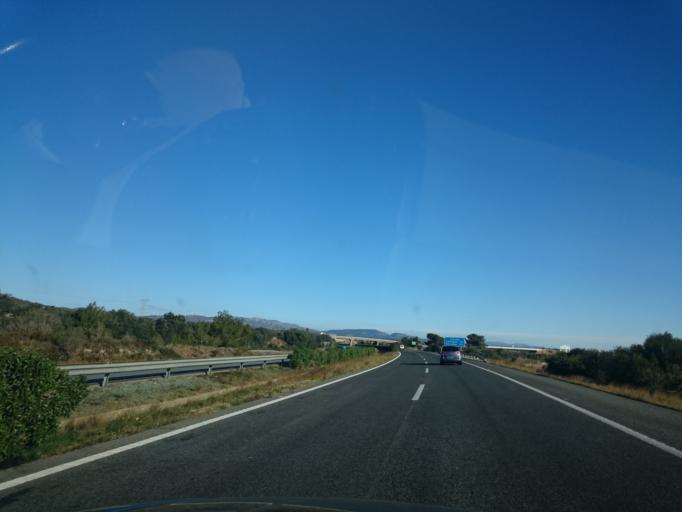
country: ES
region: Catalonia
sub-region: Provincia de Tarragona
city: Amposta
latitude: 40.7359
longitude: 0.5897
